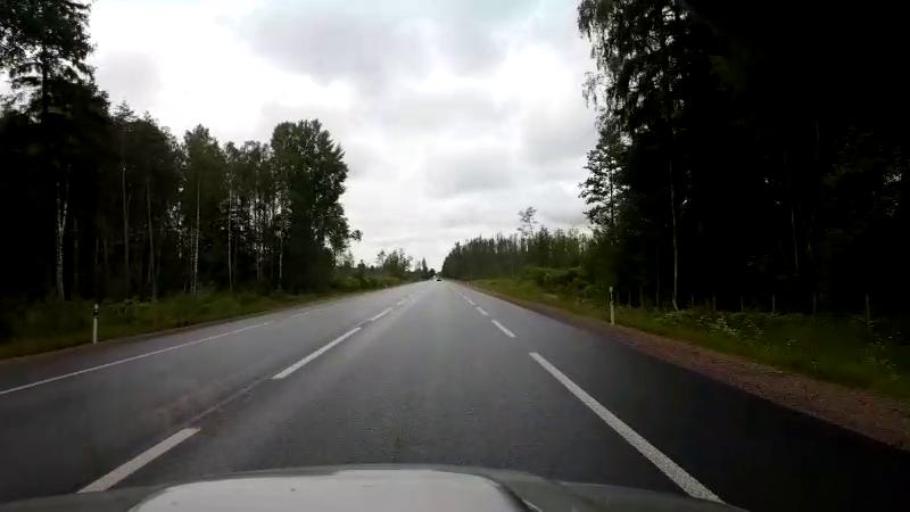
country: LV
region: Lecava
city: Iecava
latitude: 56.7045
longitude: 24.2449
